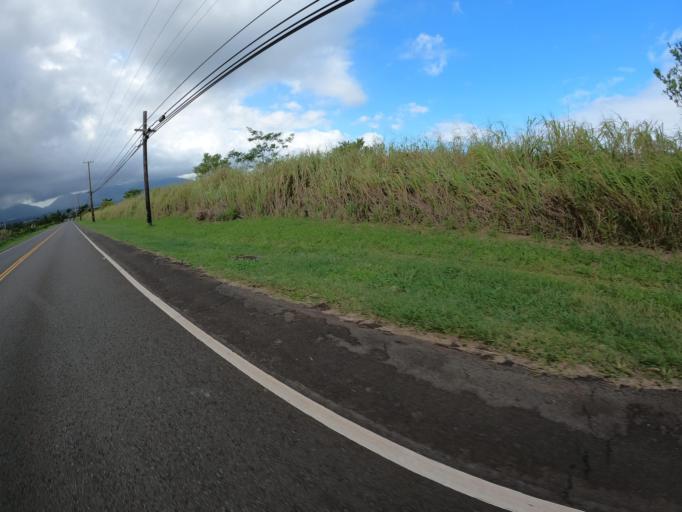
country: US
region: Hawaii
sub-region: Honolulu County
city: Whitmore Village
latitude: 21.5131
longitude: -158.0128
